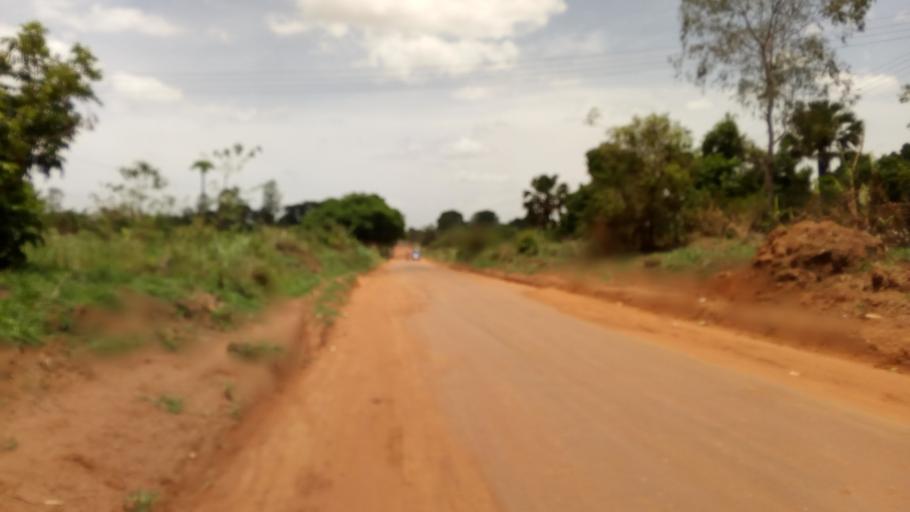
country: UG
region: Northern Region
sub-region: Gulu District
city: Gulu
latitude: 2.8040
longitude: 32.3215
